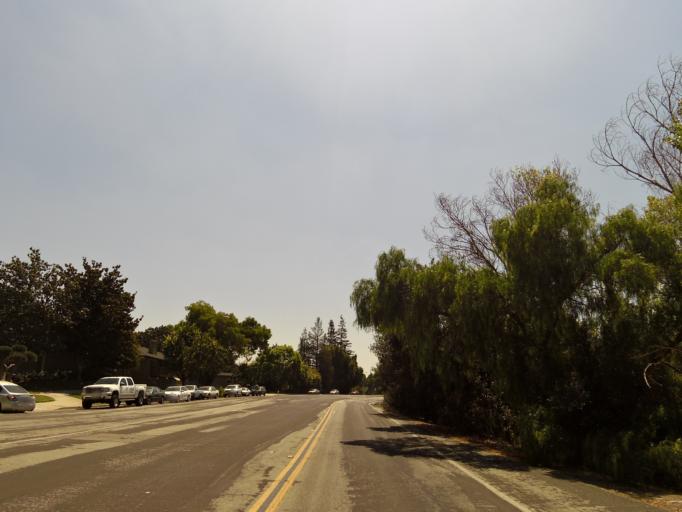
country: US
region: California
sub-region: Santa Clara County
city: Seven Trees
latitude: 37.2942
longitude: -121.8805
